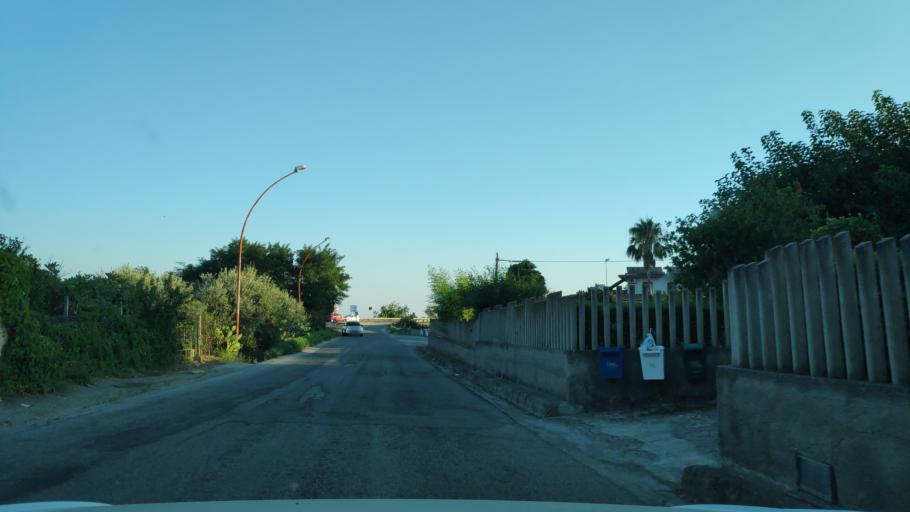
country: IT
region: Calabria
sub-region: Provincia di Reggio Calabria
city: Caulonia Marina
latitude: 38.3582
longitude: 16.4856
